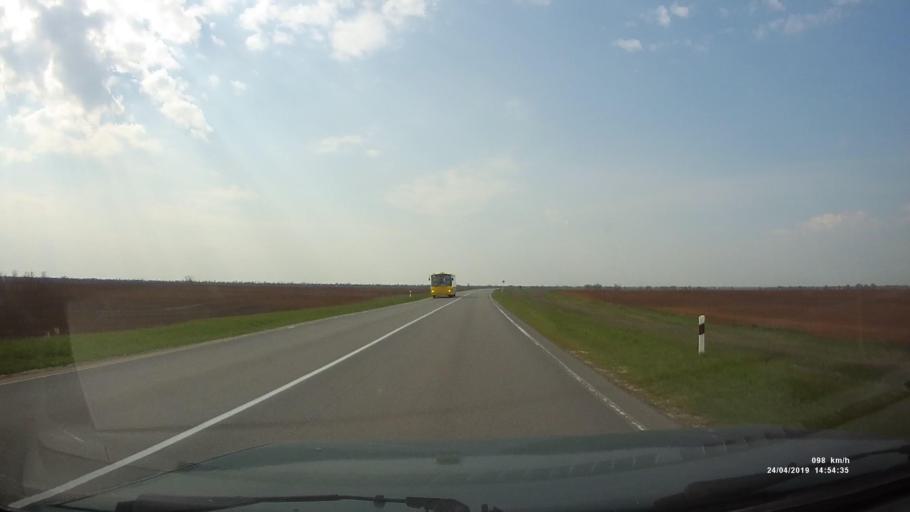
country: RU
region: Rostov
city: Remontnoye
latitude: 46.5354
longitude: 43.6363
